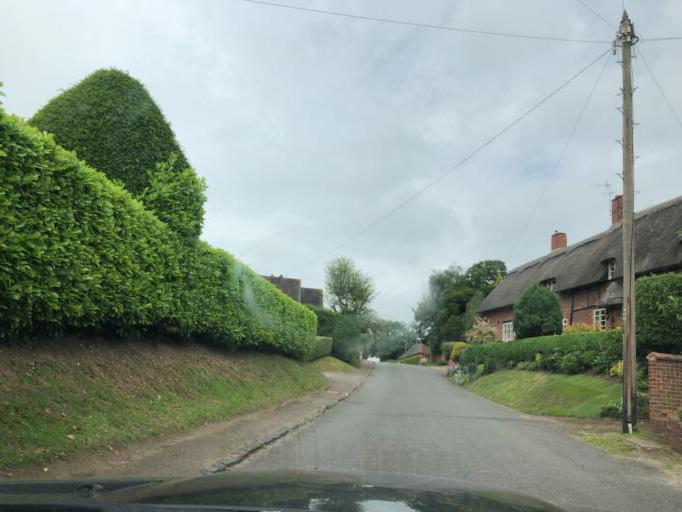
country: GB
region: England
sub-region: Warwickshire
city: Royal Leamington Spa
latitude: 52.3166
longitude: -1.5579
